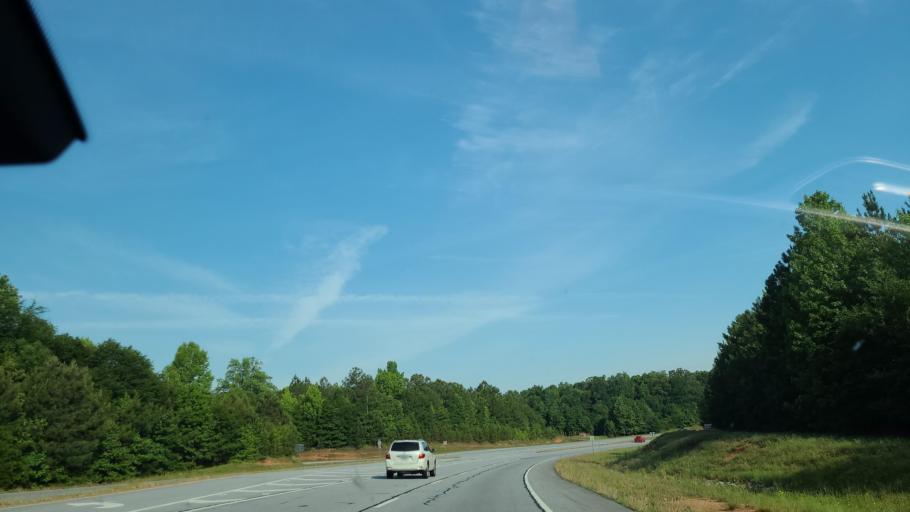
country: US
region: Georgia
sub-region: Jackson County
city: Nicholson
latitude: 34.0615
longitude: -83.4232
